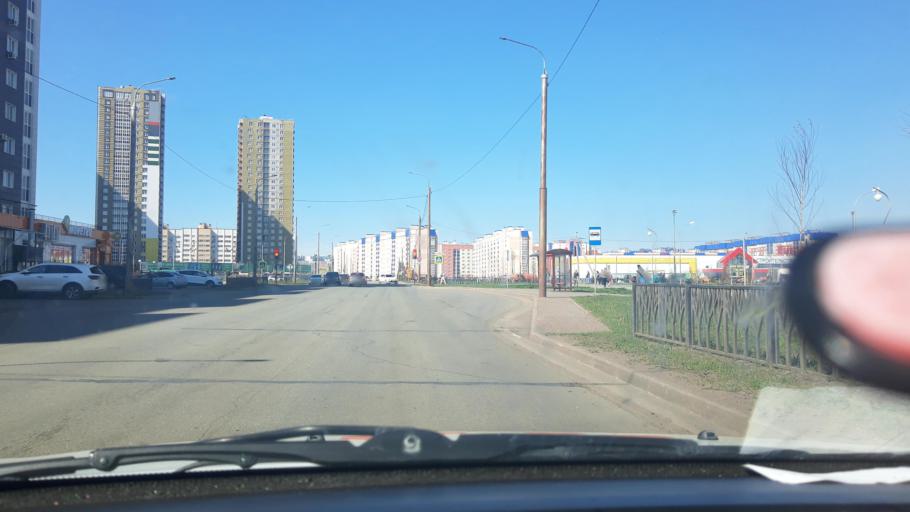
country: RU
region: Bashkortostan
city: Sterlitamak
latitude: 53.6284
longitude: 55.8960
